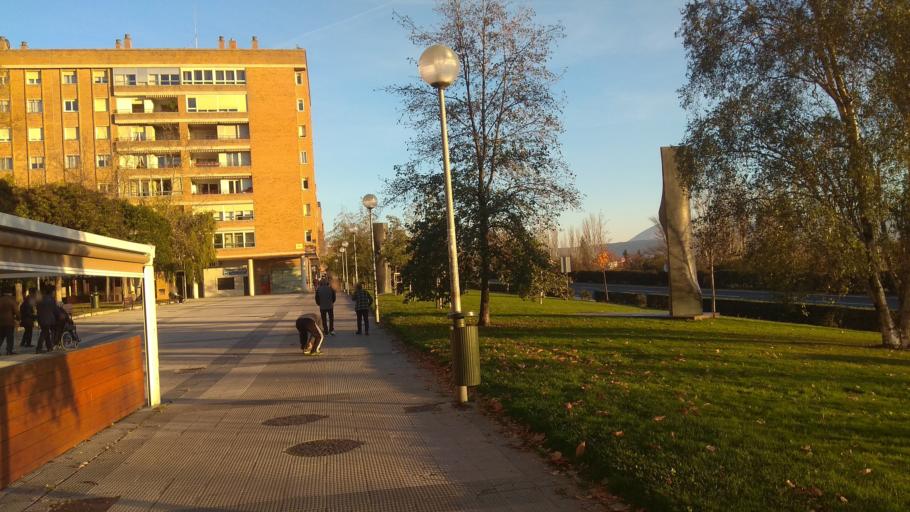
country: ES
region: Navarre
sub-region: Provincia de Navarra
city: Iturrama
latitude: 42.8037
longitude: -1.6542
